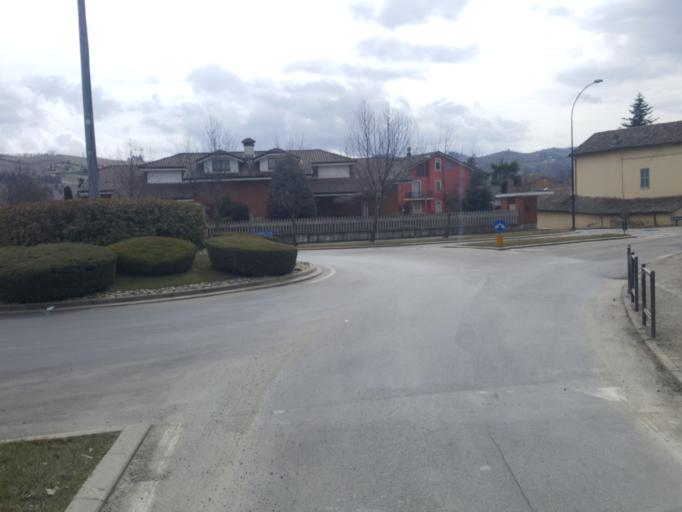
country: IT
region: Piedmont
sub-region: Provincia di Asti
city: Canelli
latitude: 44.7287
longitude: 8.2996
